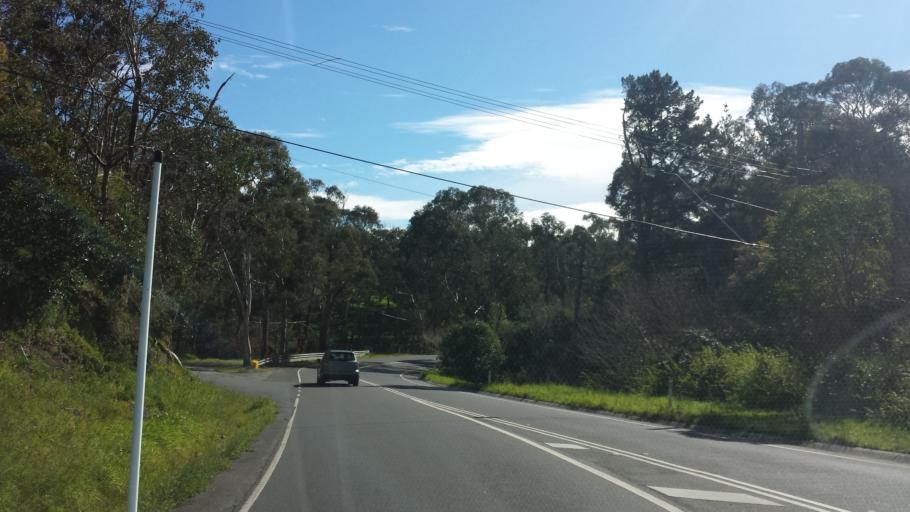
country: AU
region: Victoria
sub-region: Maroondah
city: Warranwood
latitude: -37.7739
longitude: 145.2314
